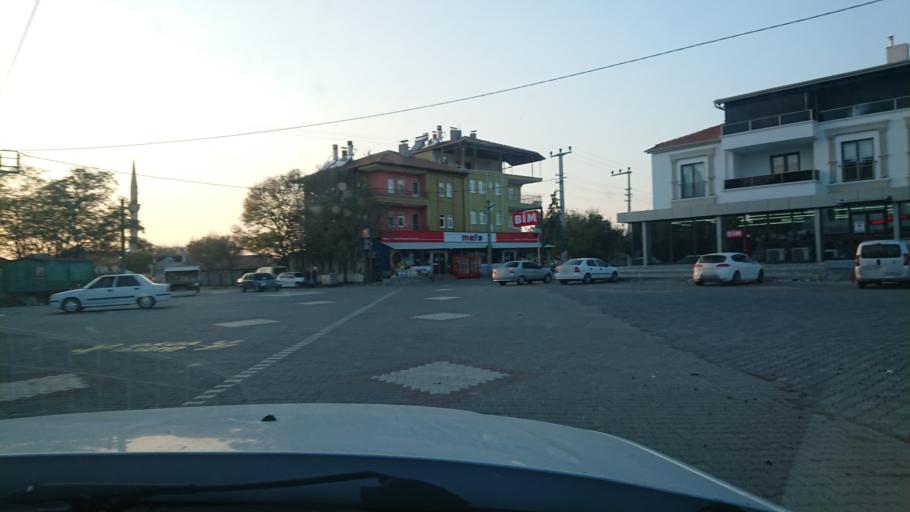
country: TR
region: Aksaray
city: Aksaray
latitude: 38.3012
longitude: 34.0711
